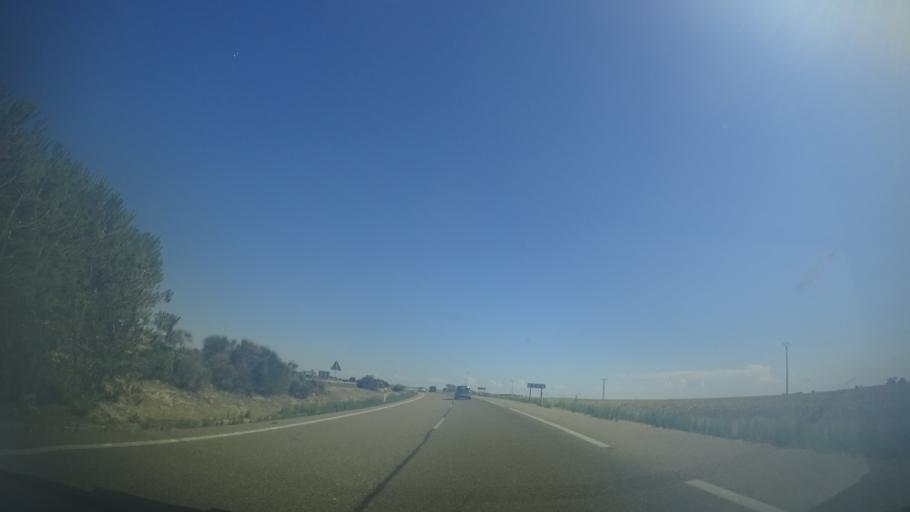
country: ES
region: Castille and Leon
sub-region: Provincia de Valladolid
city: Mota del Marques
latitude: 41.6739
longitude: -5.2030
